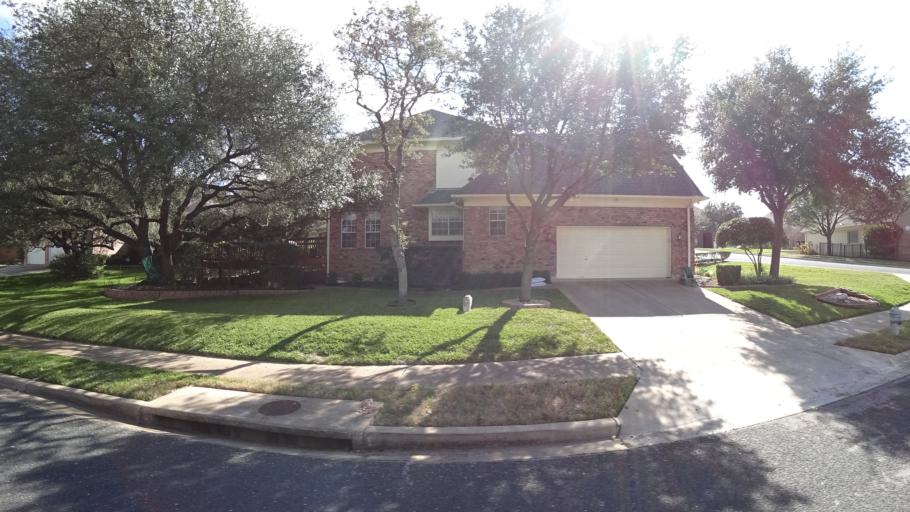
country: US
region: Texas
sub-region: Williamson County
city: Jollyville
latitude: 30.4238
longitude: -97.7863
